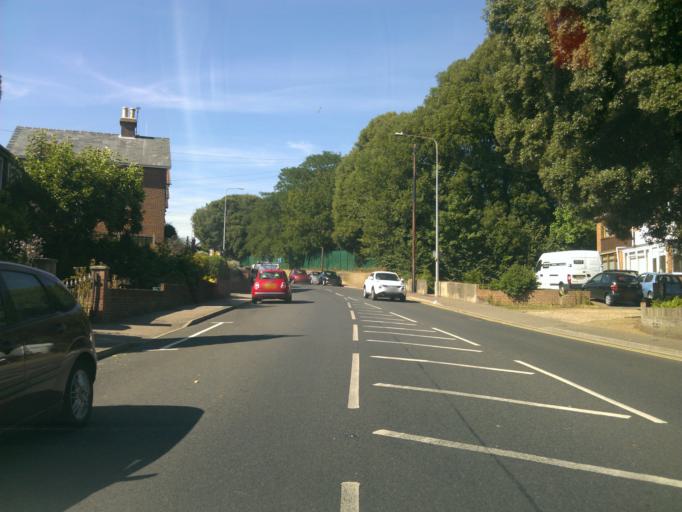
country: GB
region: England
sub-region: Essex
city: Colchester
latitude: 51.8772
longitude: 0.9081
